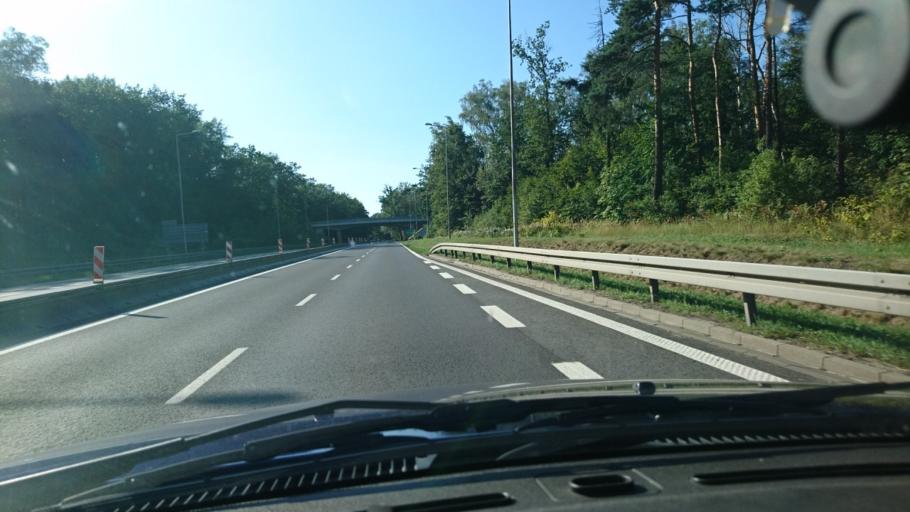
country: PL
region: Silesian Voivodeship
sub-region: Gliwice
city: Gliwice
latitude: 50.3098
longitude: 18.7165
